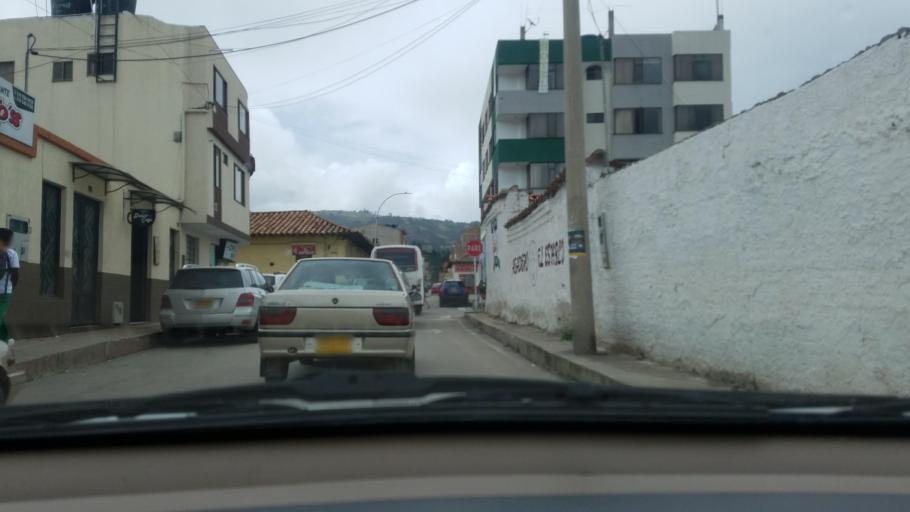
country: CO
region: Boyaca
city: Paipa
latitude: 5.7782
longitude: -73.1168
